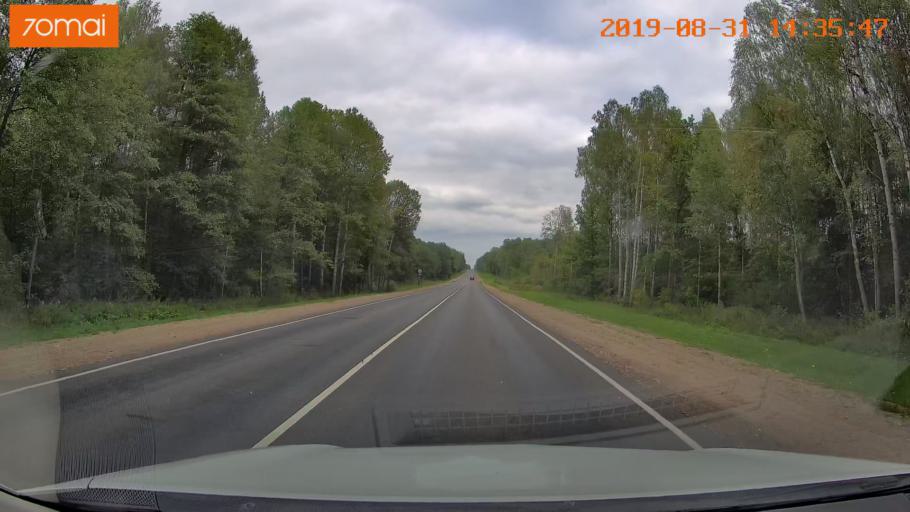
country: RU
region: Smolensk
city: Yekimovichi
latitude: 54.1652
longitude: 33.4637
